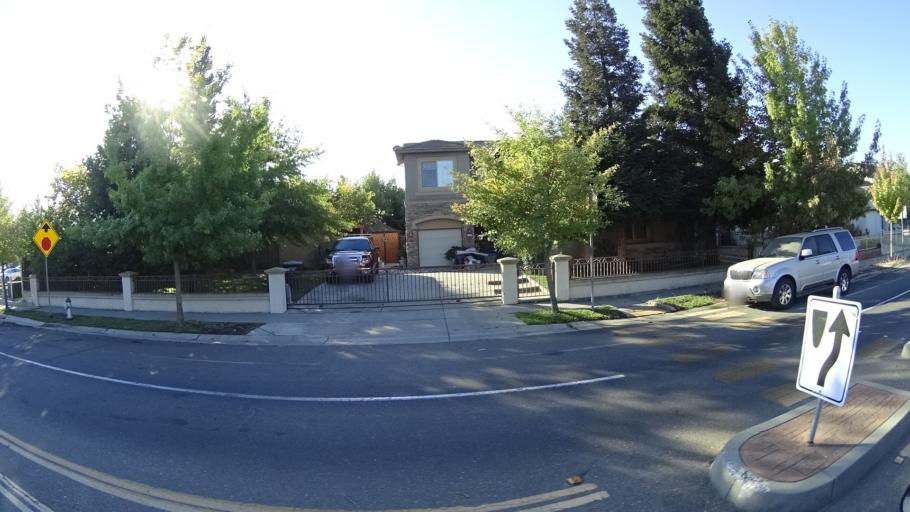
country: US
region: California
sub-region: Sacramento County
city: Parkway
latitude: 38.4770
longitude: -121.4876
